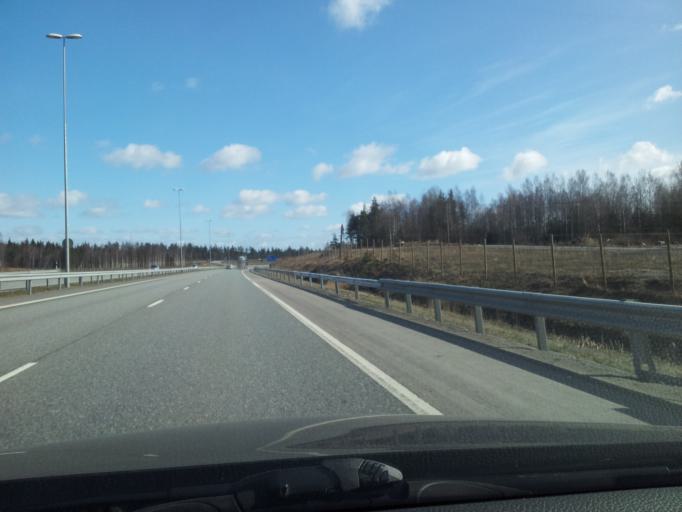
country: FI
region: Uusimaa
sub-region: Helsinki
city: Espoo
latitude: 60.1442
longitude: 24.5633
